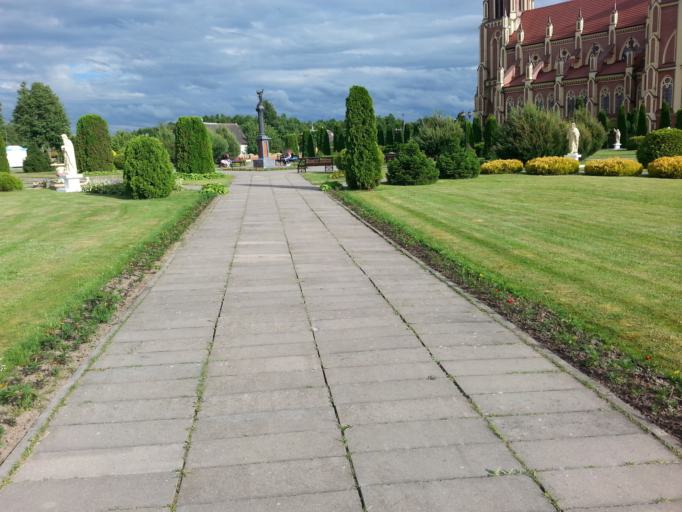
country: BY
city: Soly
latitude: 54.6880
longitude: 26.1438
